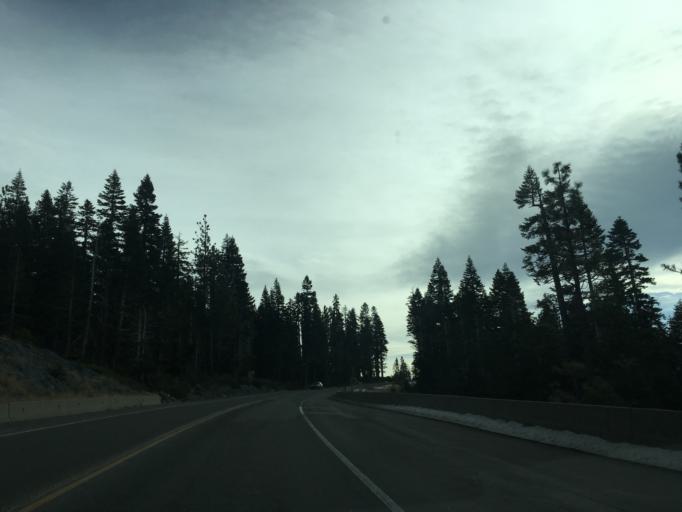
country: US
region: Nevada
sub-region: Washoe County
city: Incline Village
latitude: 39.2663
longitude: -119.9325
